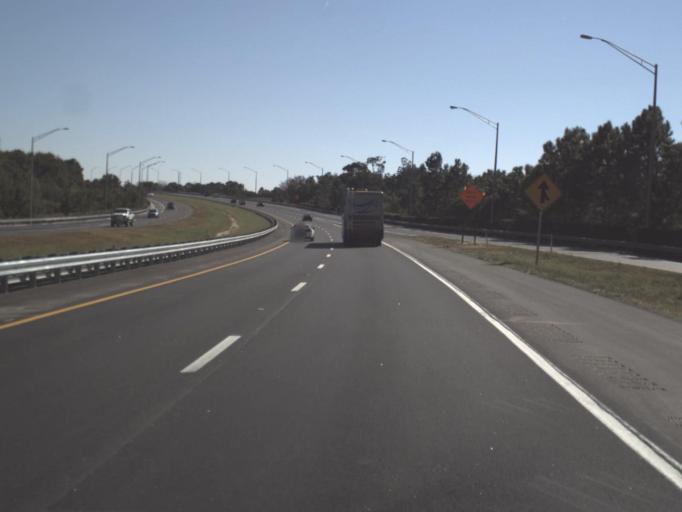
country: US
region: Florida
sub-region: Seminole County
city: Lake Mary
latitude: 28.7836
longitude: -81.3011
